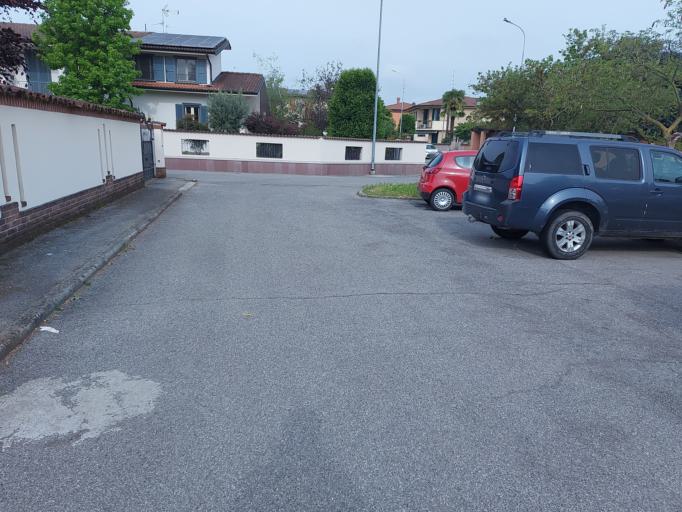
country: IT
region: Lombardy
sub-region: Provincia di Cremona
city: Castelleone
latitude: 45.2930
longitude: 9.7729
